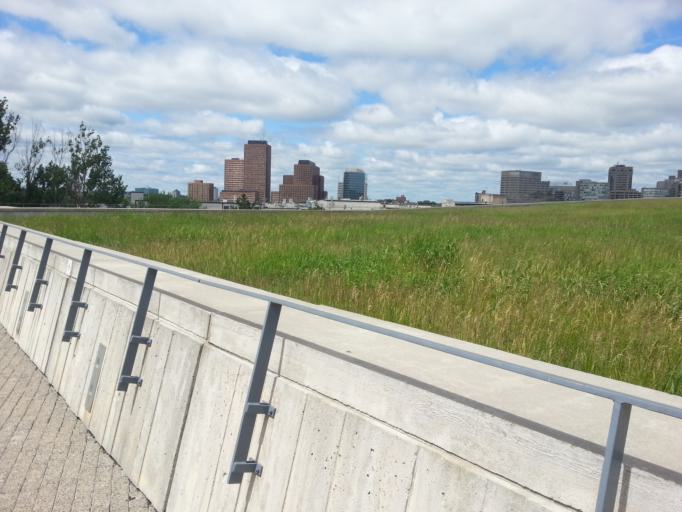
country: CA
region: Ontario
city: Ottawa
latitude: 45.4170
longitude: -75.7174
